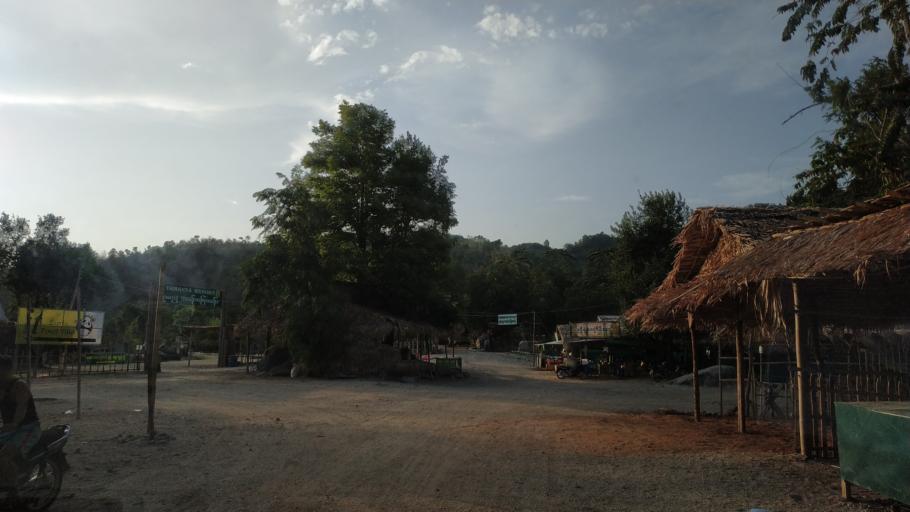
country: MM
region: Mon
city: Kyaikto
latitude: 17.4366
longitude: 97.0397
